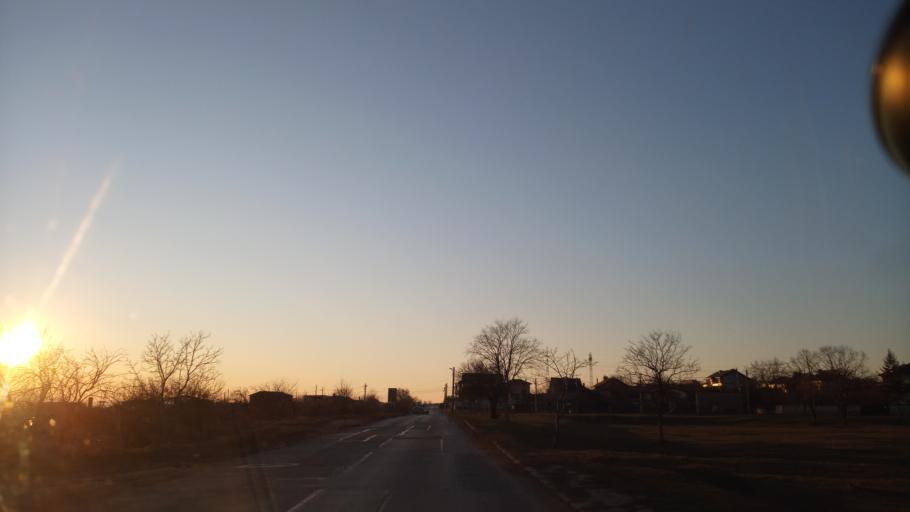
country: BG
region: Sofia-Capital
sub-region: Stolichna Obshtina
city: Bukhovo
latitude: 42.7798
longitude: 23.5169
